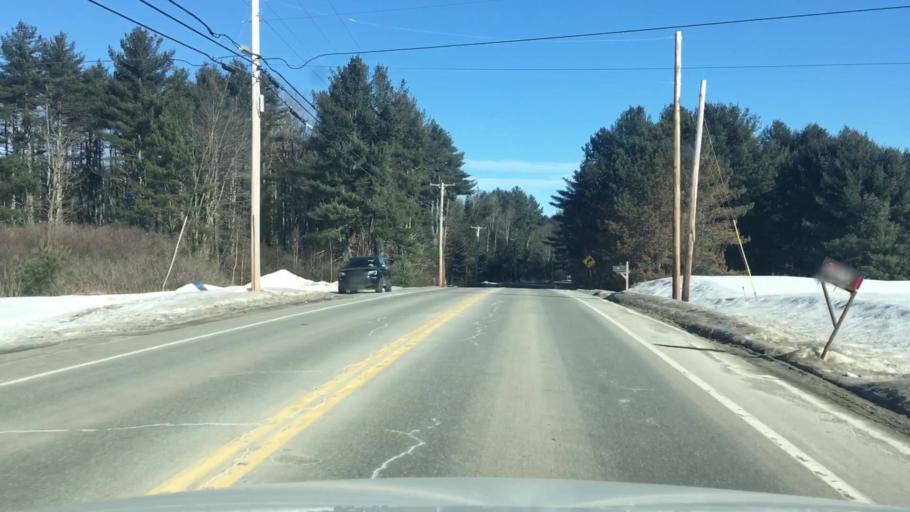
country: US
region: Maine
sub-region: Androscoggin County
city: Lisbon Falls
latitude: 43.9876
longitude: -70.0973
